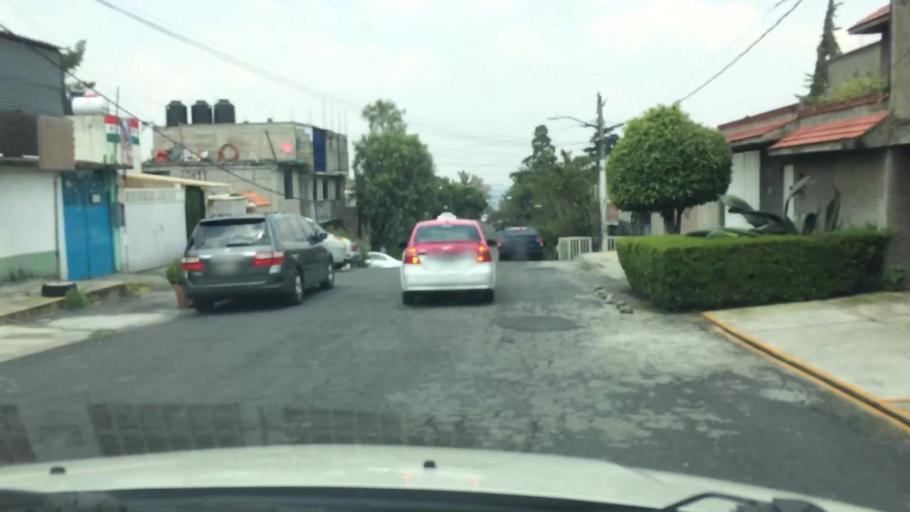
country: MX
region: Mexico City
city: Magdalena Contreras
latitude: 19.2937
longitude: -99.2252
